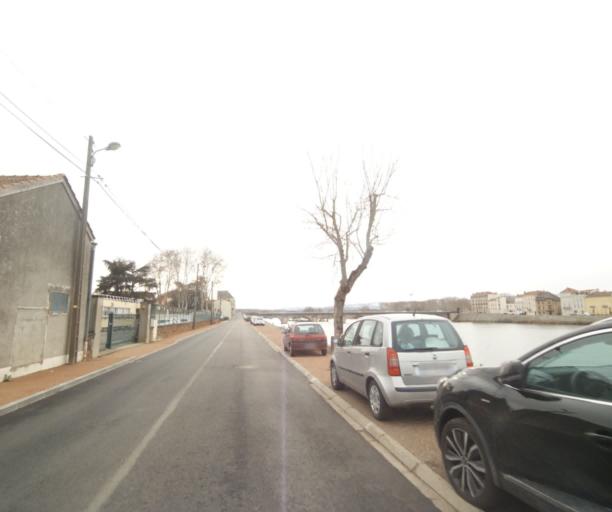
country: FR
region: Rhone-Alpes
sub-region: Departement de la Loire
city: Le Coteau
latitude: 46.0345
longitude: 4.0844
